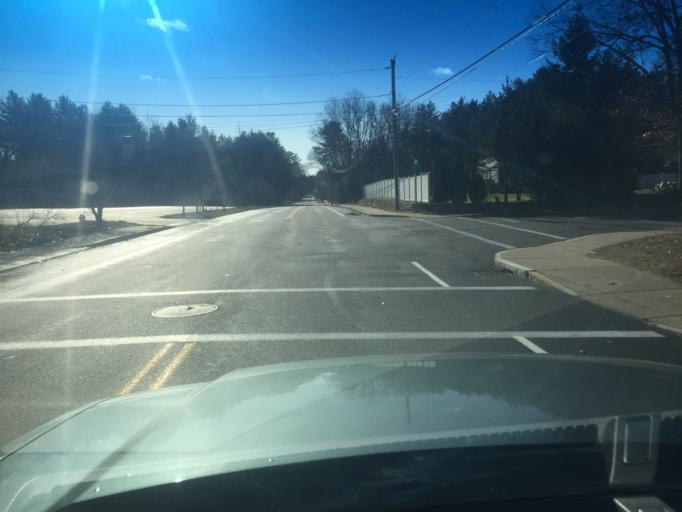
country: US
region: Massachusetts
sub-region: Norfolk County
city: Medway
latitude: 42.1272
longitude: -71.4313
